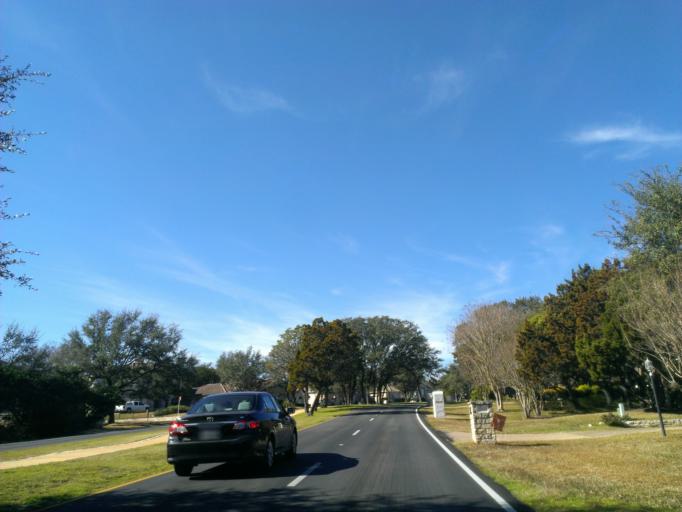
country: US
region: Texas
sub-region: Travis County
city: Lakeway
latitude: 30.3567
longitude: -97.9738
